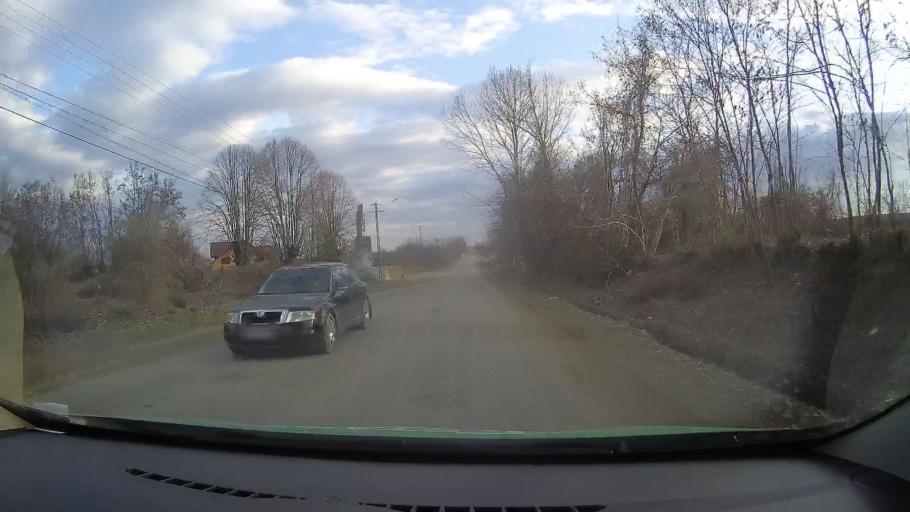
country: RO
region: Dambovita
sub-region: Municipiul Moreni
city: Moreni
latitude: 44.9613
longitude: 25.6572
